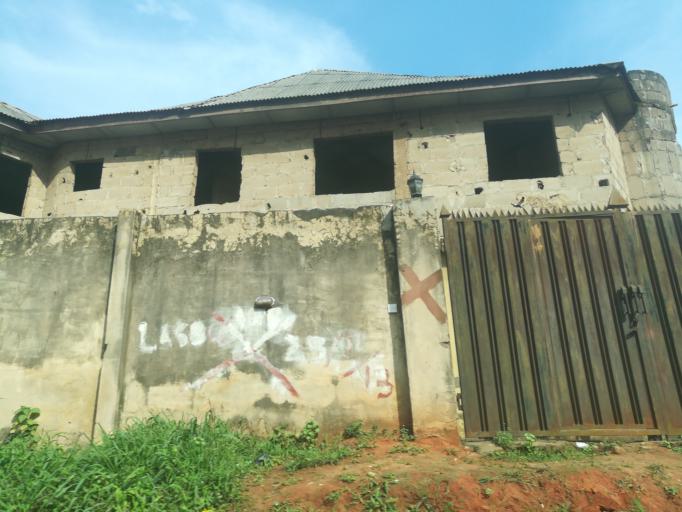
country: NG
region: Lagos
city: Ikorodu
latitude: 6.6288
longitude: 3.5100
